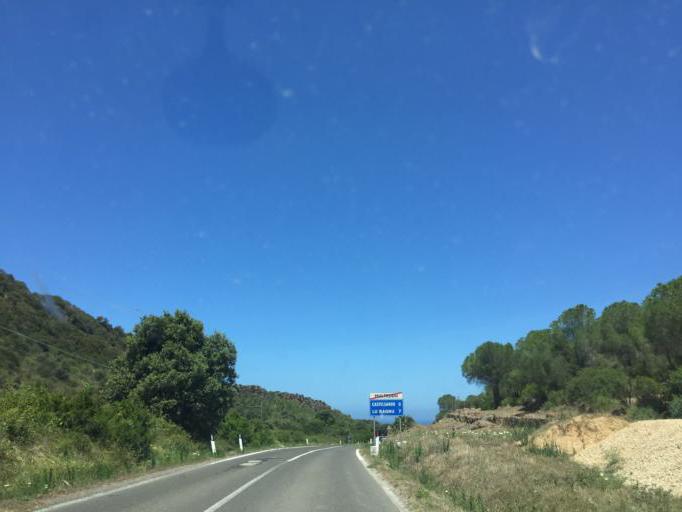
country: IT
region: Sardinia
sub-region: Provincia di Sassari
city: Castelsardo
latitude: 40.8982
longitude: 8.7427
